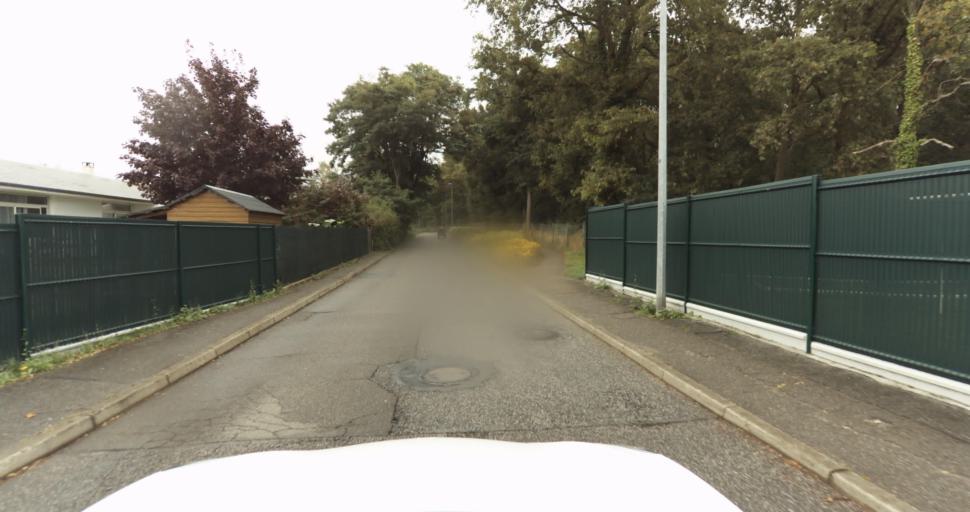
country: FR
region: Haute-Normandie
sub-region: Departement de l'Eure
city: Evreux
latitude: 49.0360
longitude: 1.1357
